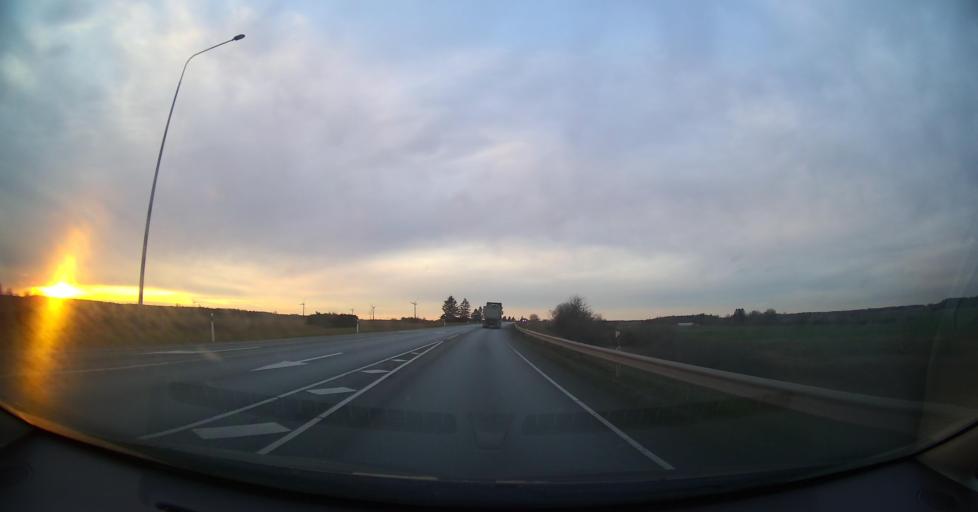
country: EE
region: Ida-Virumaa
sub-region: Aseri vald
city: Aseri
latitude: 59.4419
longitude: 26.8072
